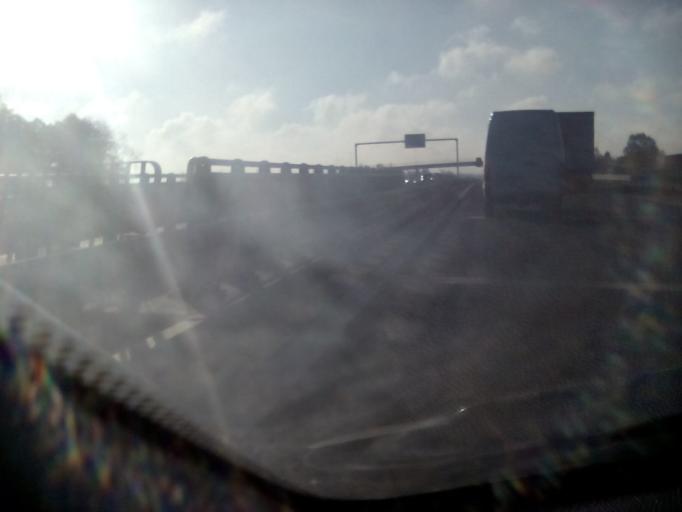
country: PL
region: Masovian Voivodeship
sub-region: Powiat grojecki
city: Grojec
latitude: 51.8164
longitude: 20.8835
